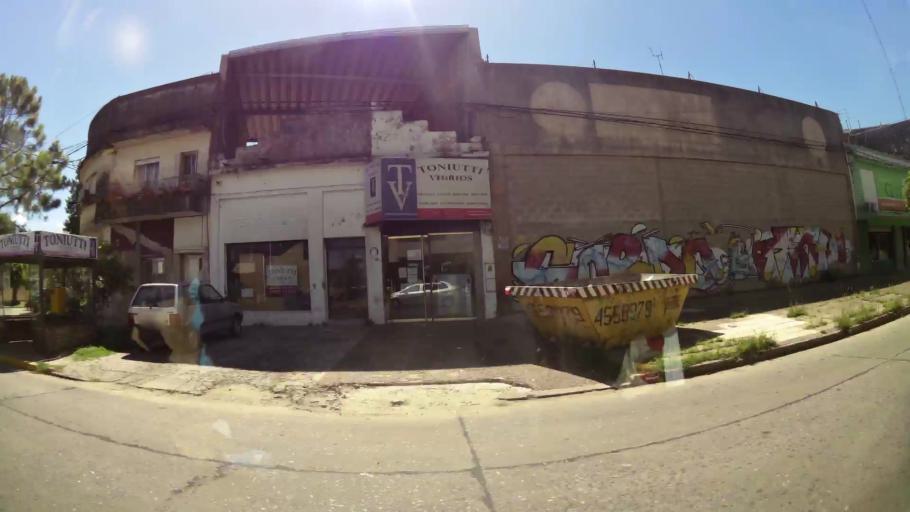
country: AR
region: Santa Fe
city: Santa Fe de la Vera Cruz
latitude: -31.6299
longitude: -60.6927
